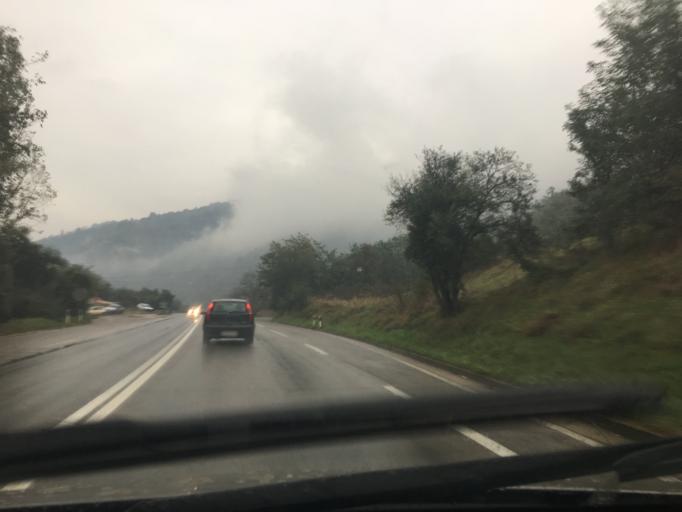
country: RS
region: Central Serbia
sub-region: Pcinjski Okrug
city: Vladicin Han
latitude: 42.7734
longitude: 22.0912
